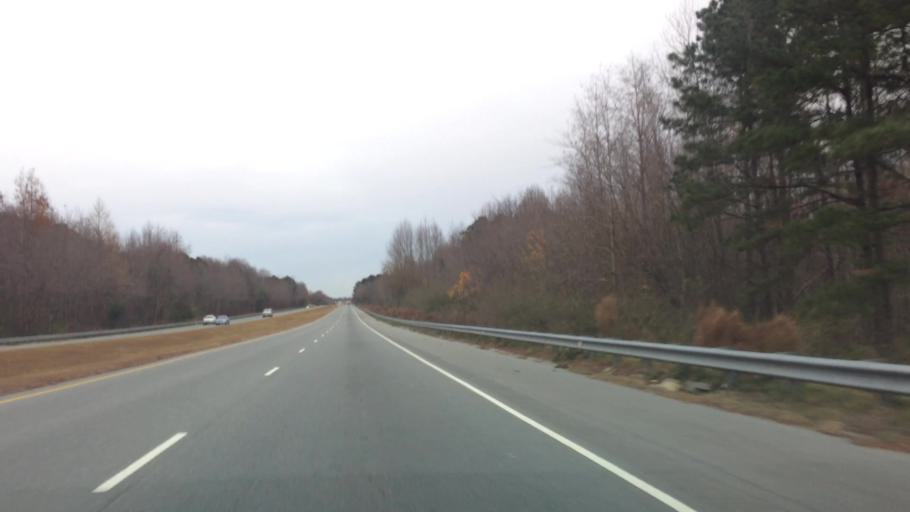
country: US
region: North Carolina
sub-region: Wayne County
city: Mount Olive
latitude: 35.1360
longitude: -78.1389
